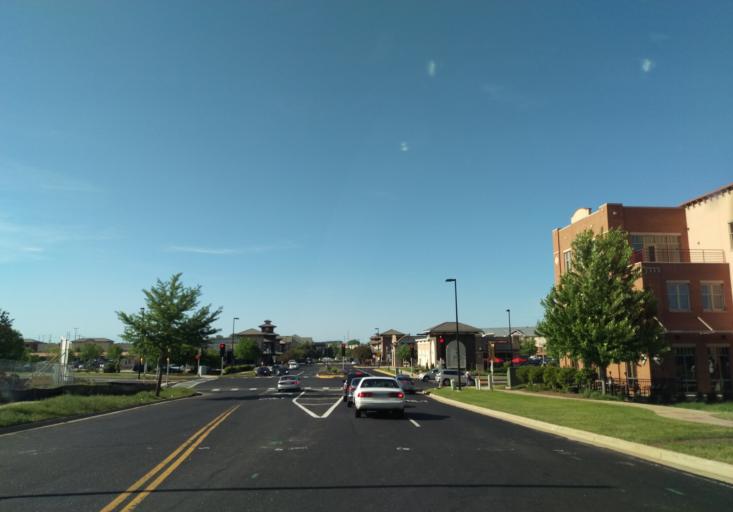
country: US
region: Wisconsin
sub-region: Dane County
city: Middleton
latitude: 43.0894
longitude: -89.5271
